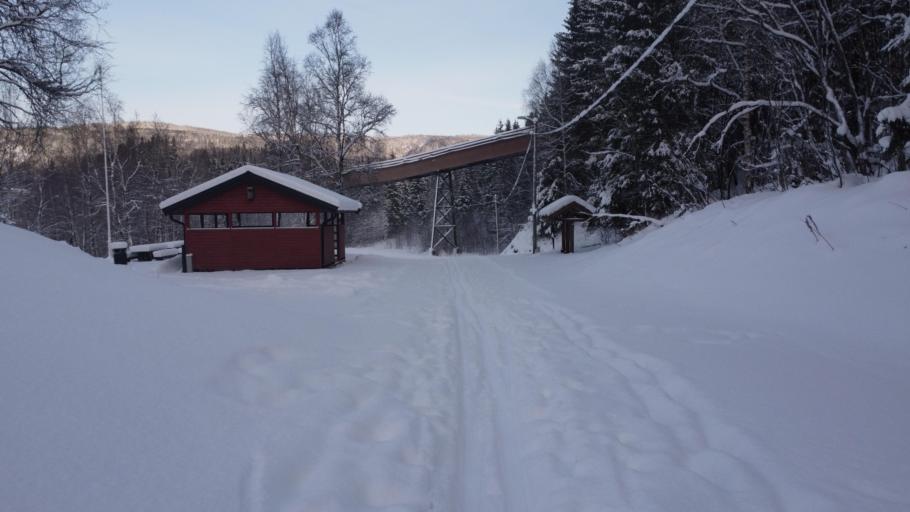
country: NO
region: Nordland
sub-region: Rana
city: Mo i Rana
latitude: 66.3148
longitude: 14.1719
